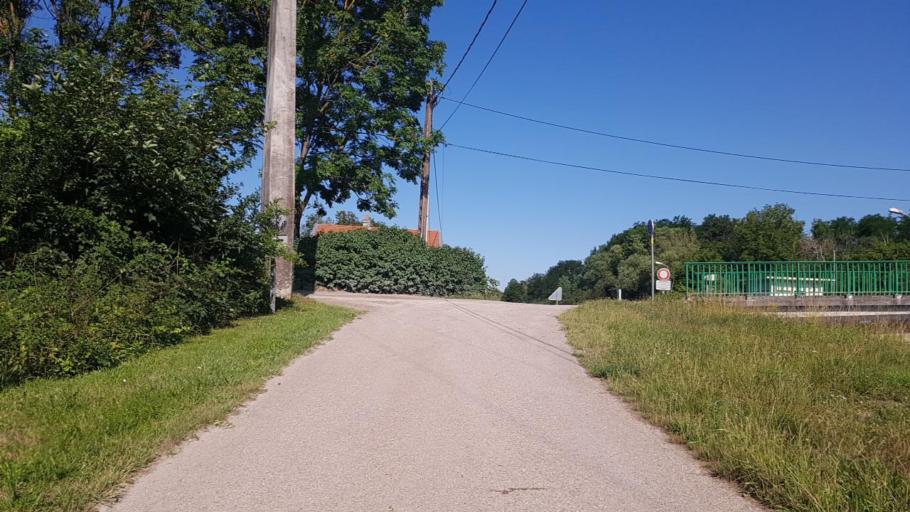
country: FR
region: Lorraine
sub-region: Departement de Meurthe-et-Moselle
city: Ecrouves
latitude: 48.6739
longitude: 5.8182
